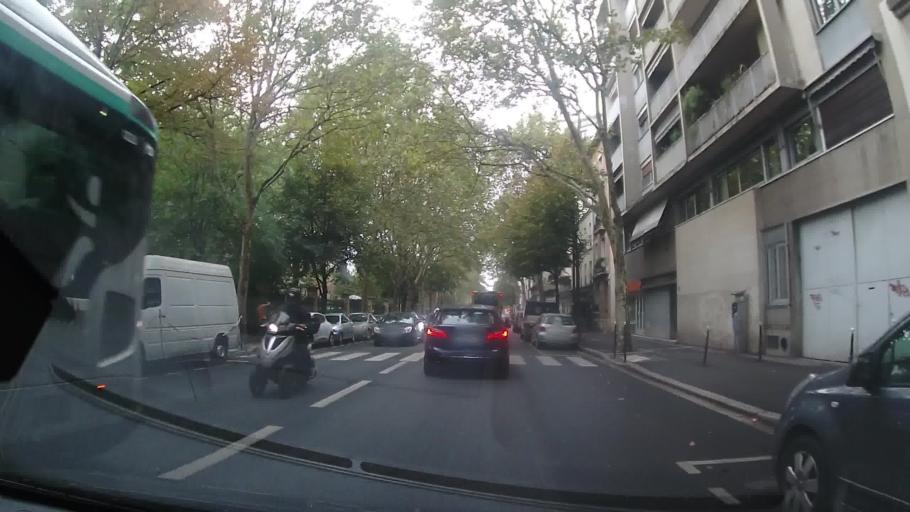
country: FR
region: Ile-de-France
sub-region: Departement des Hauts-de-Seine
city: Clichy
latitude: 48.9041
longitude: 2.3128
